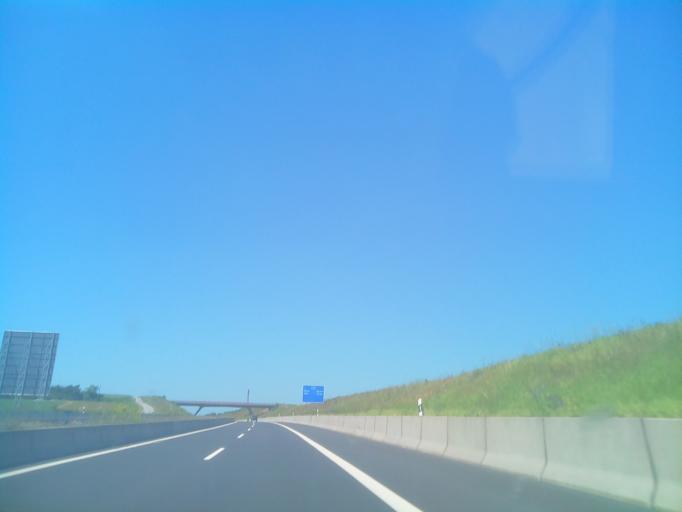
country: DE
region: Bavaria
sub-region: Regierungsbezirk Unterfranken
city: Rannungen
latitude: 50.2048
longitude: 10.2190
